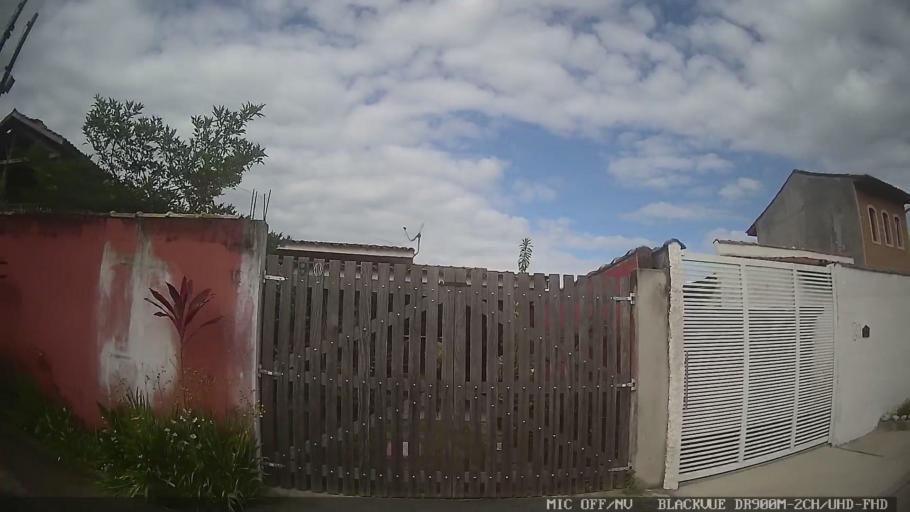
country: BR
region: Sao Paulo
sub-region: Sao Sebastiao
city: Sao Sebastiao
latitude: -23.7014
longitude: -45.4355
